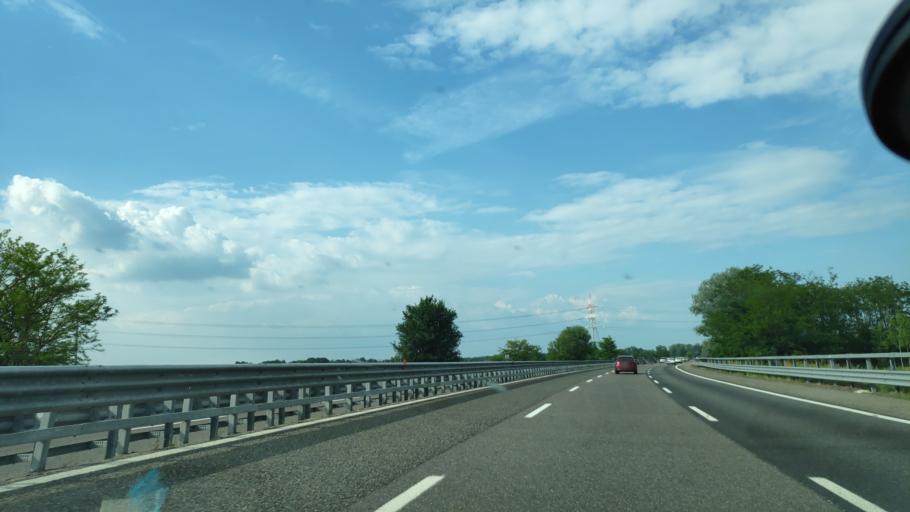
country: IT
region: Lombardy
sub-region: Provincia di Pavia
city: Zerbolo
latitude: 45.2178
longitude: 9.0184
